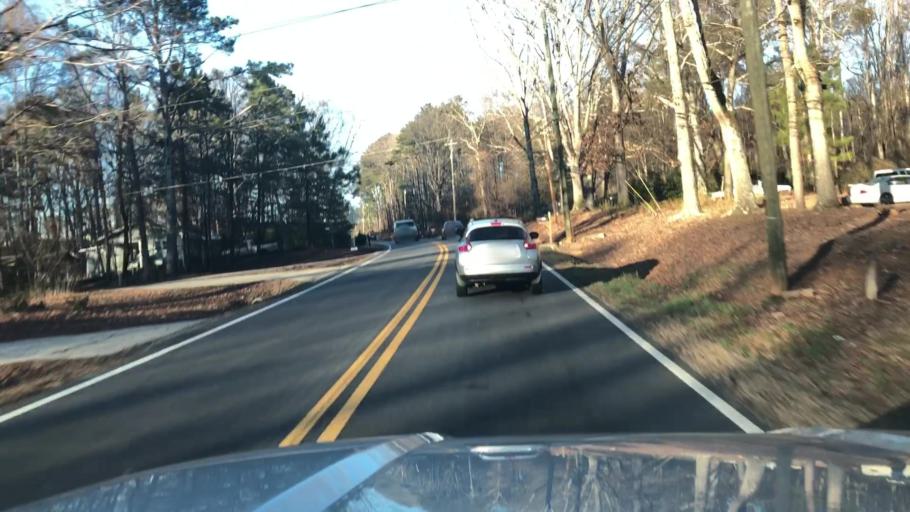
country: US
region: Georgia
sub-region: Cherokee County
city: Holly Springs
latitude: 34.2004
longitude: -84.5244
